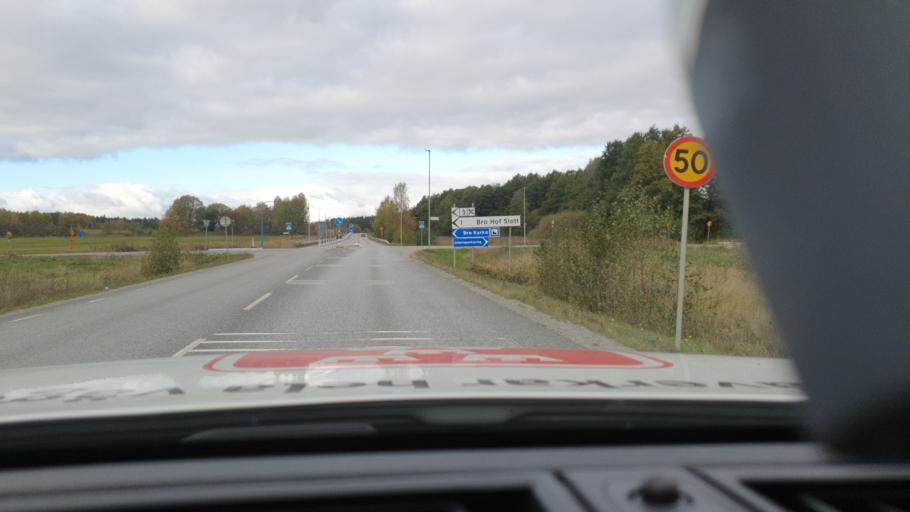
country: SE
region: Stockholm
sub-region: Upplands-Bro Kommun
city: Bro
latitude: 59.5093
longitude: 17.6310
